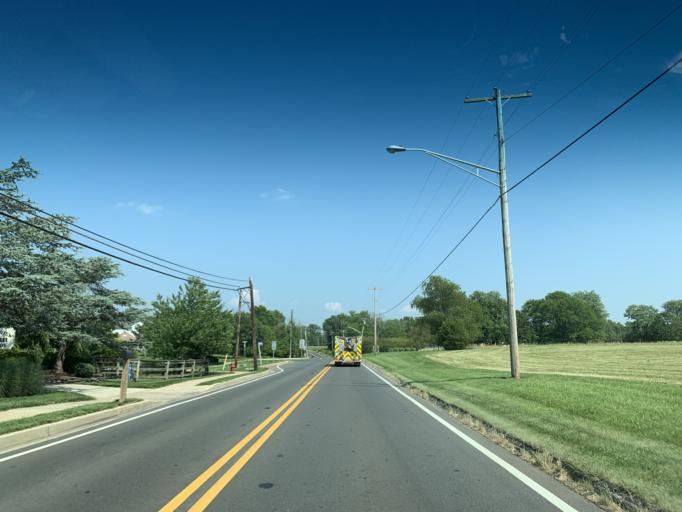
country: US
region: Maryland
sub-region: Montgomery County
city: Poolesville
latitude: 39.1331
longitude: -77.3987
